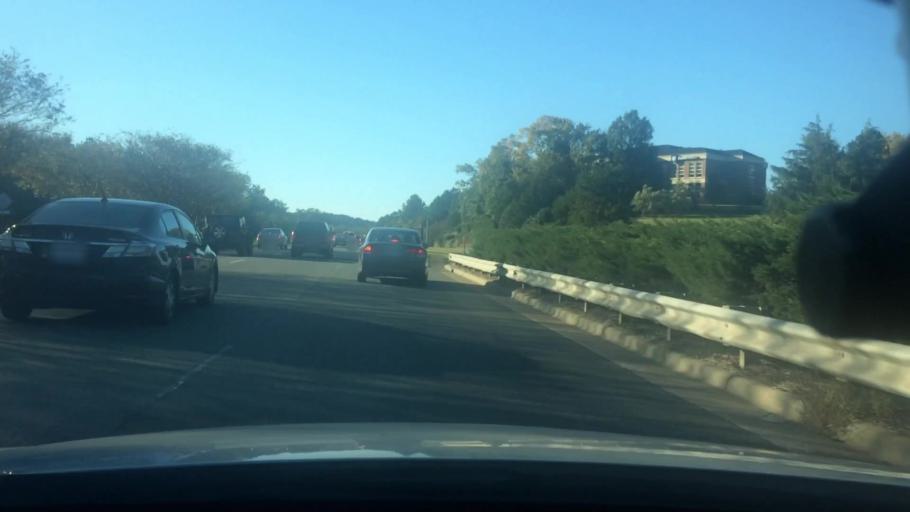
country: US
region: North Carolina
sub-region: Orange County
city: Chapel Hill
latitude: 35.9043
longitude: -79.0138
